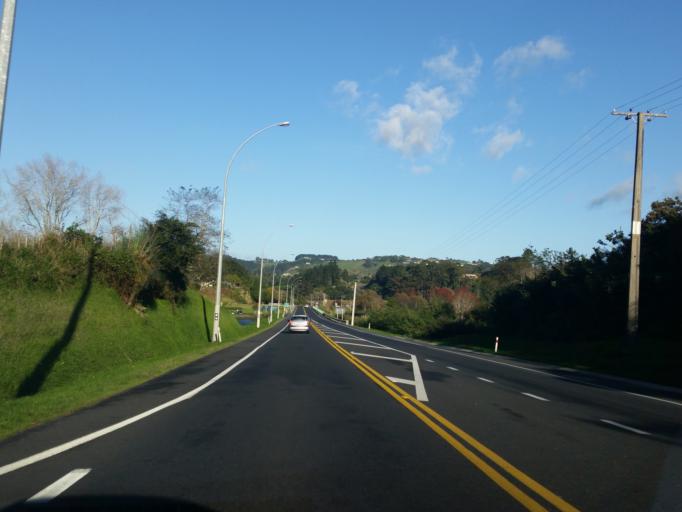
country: NZ
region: Bay of Plenty
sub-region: Tauranga City
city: Tauranga
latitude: -37.6974
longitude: 176.0976
